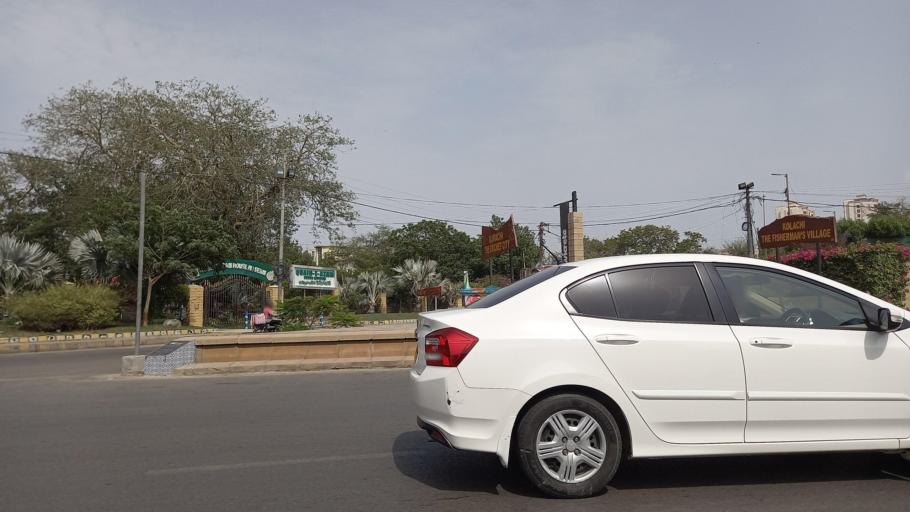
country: PK
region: Sindh
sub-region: Karachi District
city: Karachi
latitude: 24.8509
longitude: 67.0320
